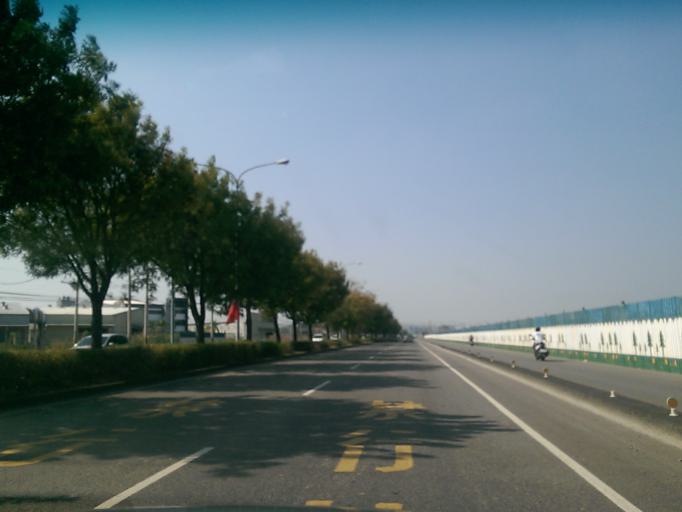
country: TW
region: Taiwan
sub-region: Taichung City
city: Taichung
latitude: 24.1211
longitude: 120.6363
